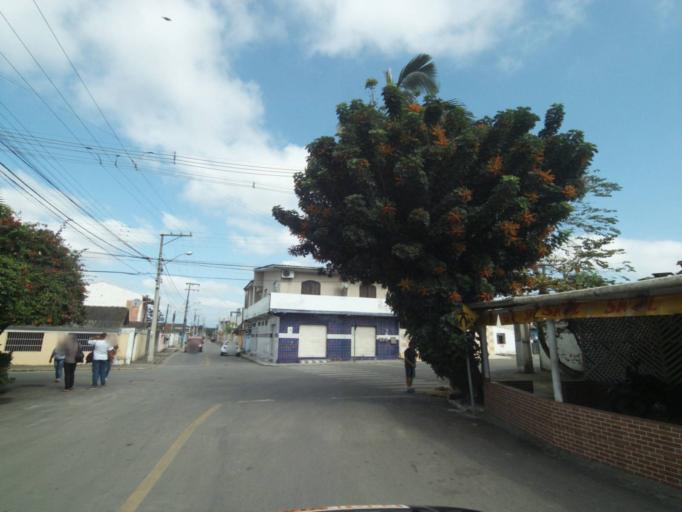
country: BR
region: Parana
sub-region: Paranagua
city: Paranagua
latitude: -25.5264
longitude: -48.5105
